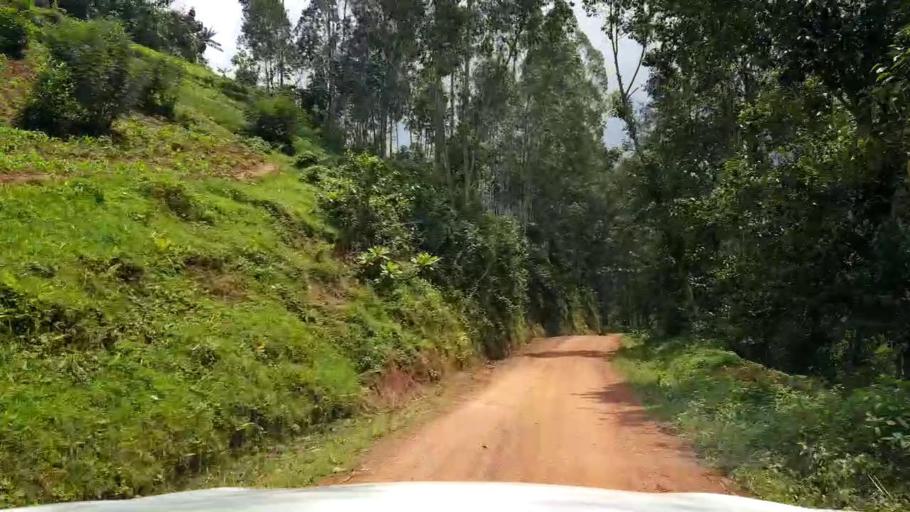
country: UG
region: Western Region
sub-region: Kabale District
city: Kabale
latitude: -1.4245
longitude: 29.8636
